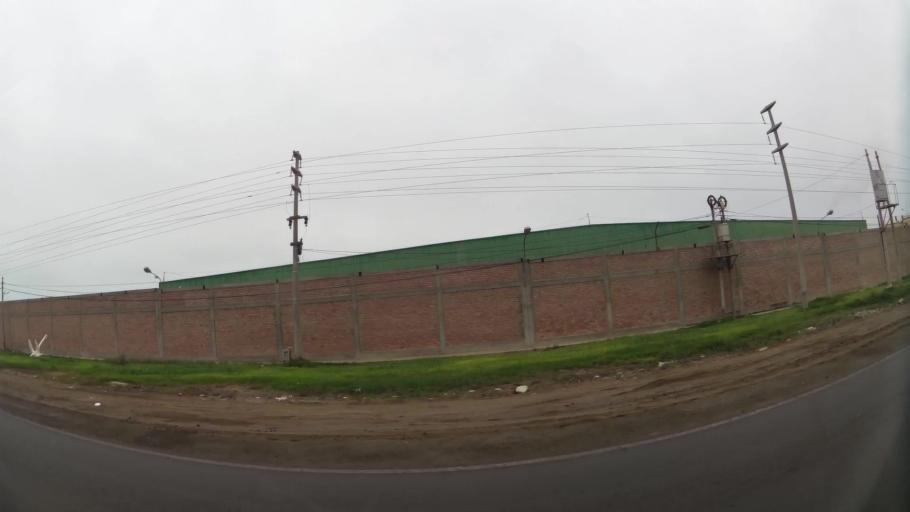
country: PE
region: Ica
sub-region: Provincia de Pisco
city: Paracas
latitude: -13.7909
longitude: -76.2394
